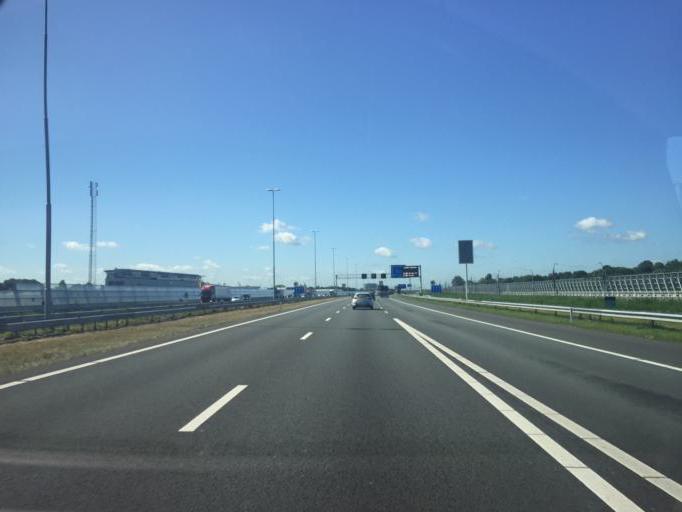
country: NL
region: South Holland
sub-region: Gemeente Kaag en Braassem
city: Oude Wetering
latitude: 52.2117
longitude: 4.6246
